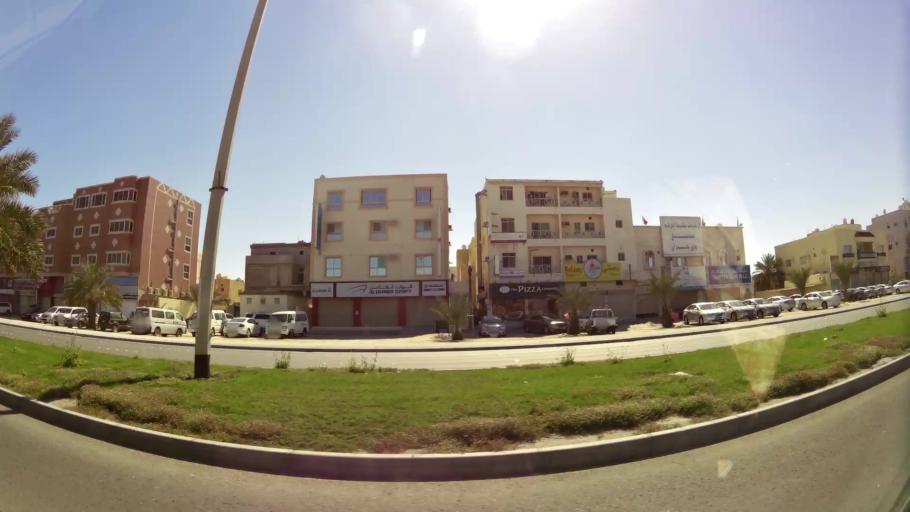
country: BH
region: Muharraq
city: Al Hadd
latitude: 26.2594
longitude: 50.6456
